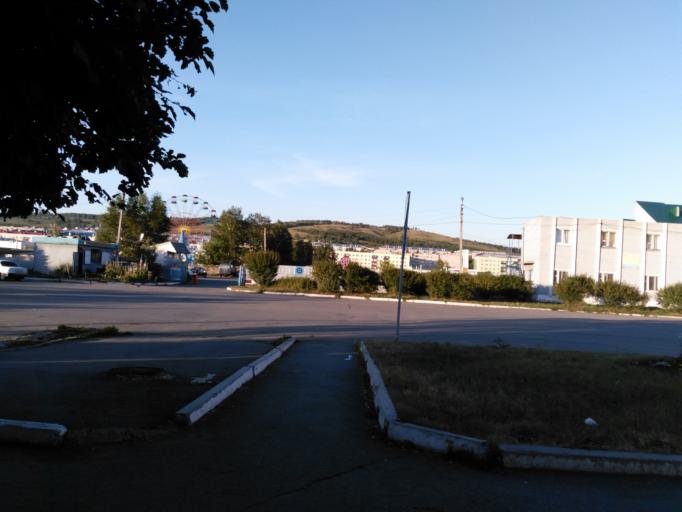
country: RU
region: Bashkortostan
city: Uchaly
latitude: 54.3192
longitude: 59.3714
